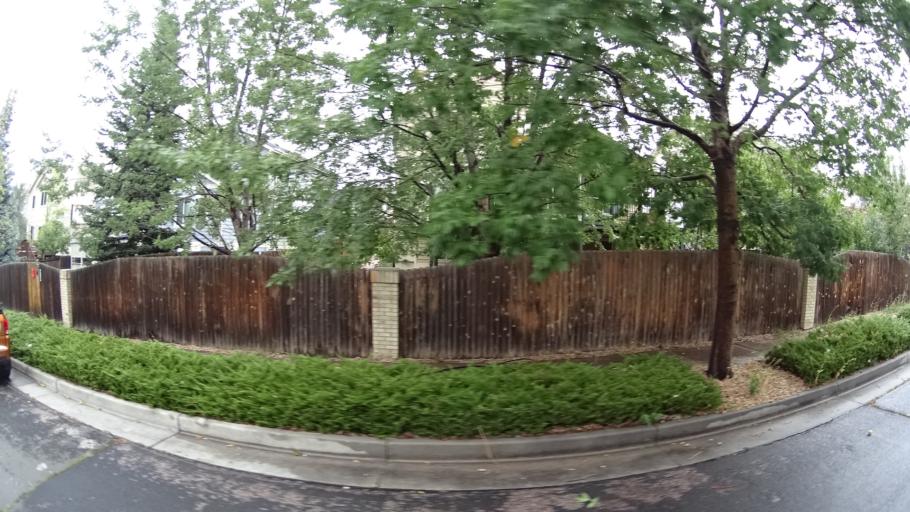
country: US
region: Colorado
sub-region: El Paso County
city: Cimarron Hills
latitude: 38.9277
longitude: -104.7615
